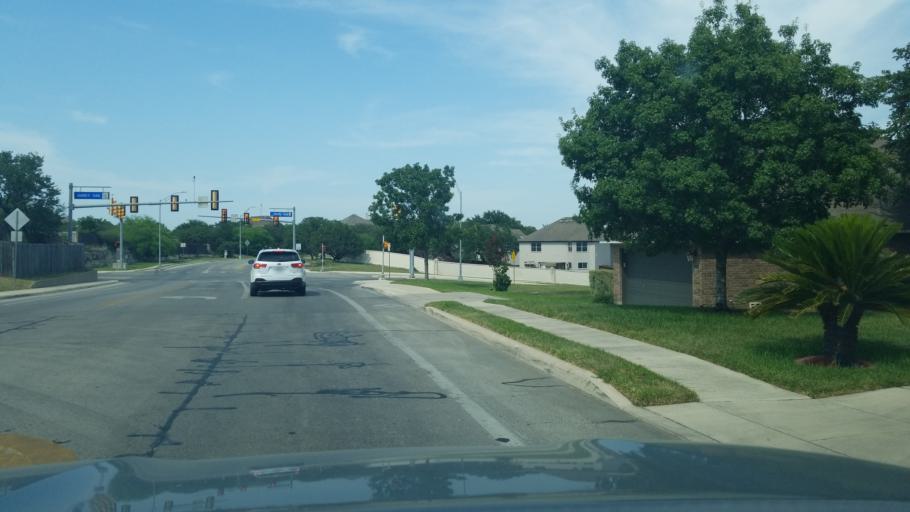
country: US
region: Texas
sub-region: Bexar County
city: Hollywood Park
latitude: 29.6358
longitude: -98.4854
